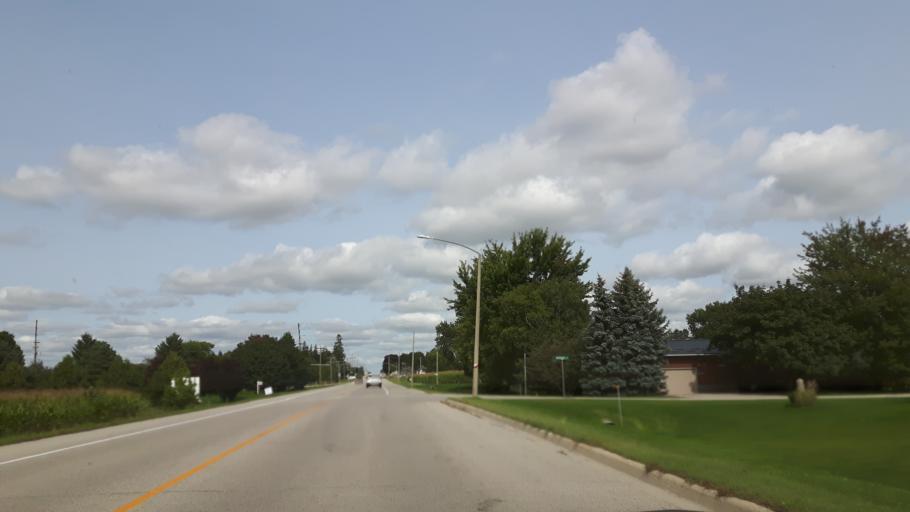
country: CA
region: Ontario
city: Huron East
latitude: 43.5599
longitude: -81.3878
